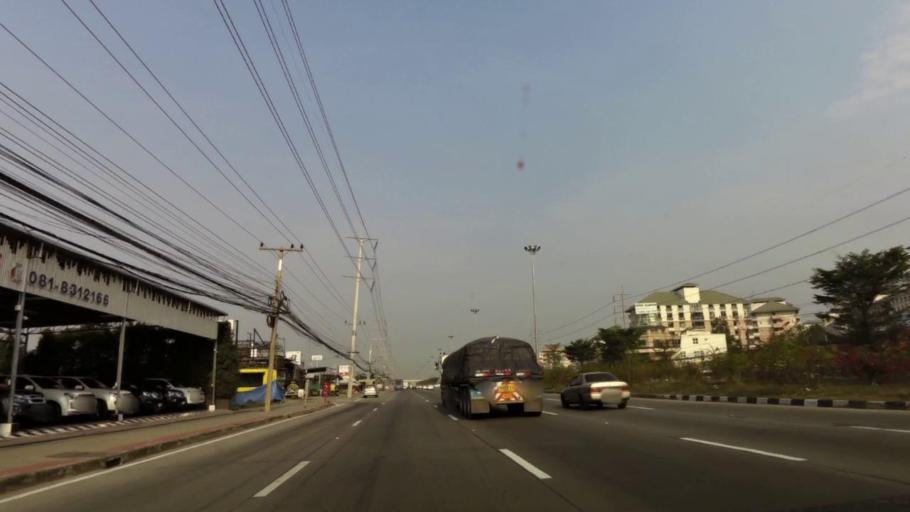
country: TH
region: Phra Nakhon Si Ayutthaya
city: Phra Nakhon Si Ayutthaya
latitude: 14.3256
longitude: 100.6279
